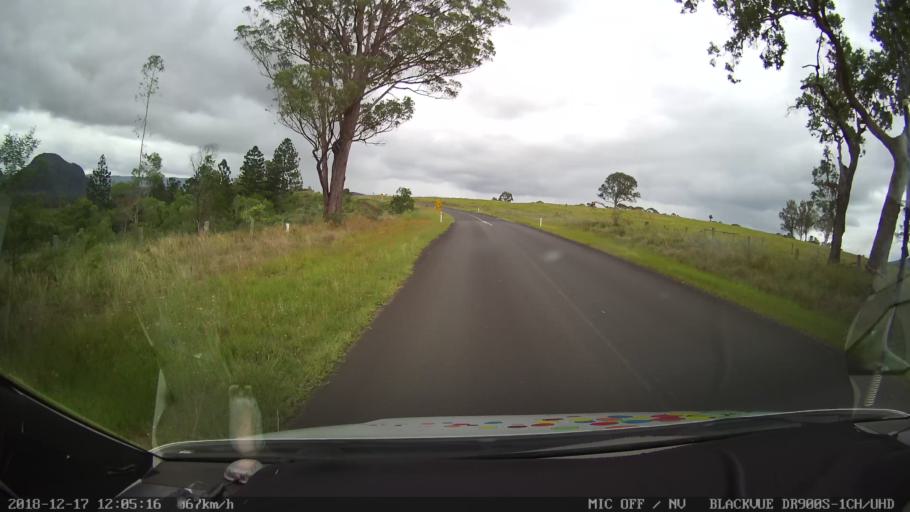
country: AU
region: New South Wales
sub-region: Kyogle
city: Kyogle
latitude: -28.4940
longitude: 152.5672
